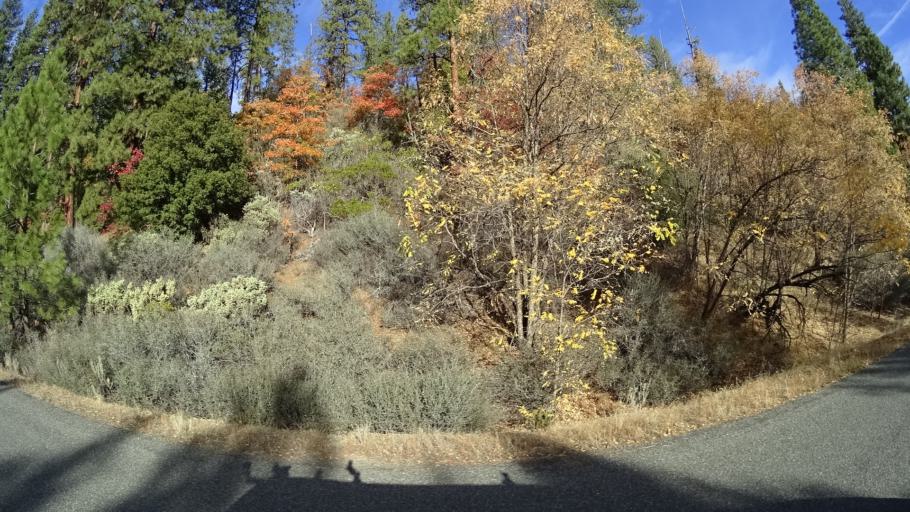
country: US
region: California
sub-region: Siskiyou County
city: Yreka
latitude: 41.6845
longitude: -122.8235
